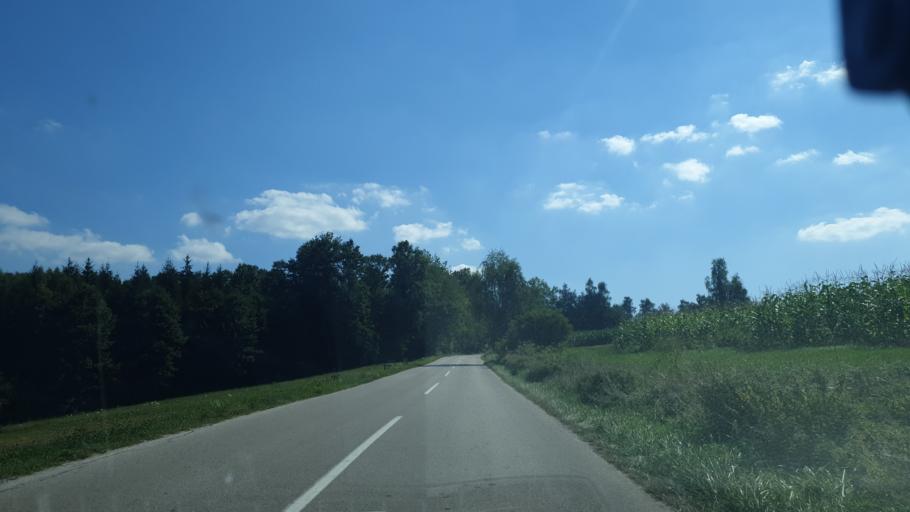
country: RS
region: Central Serbia
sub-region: Zlatiborski Okrug
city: Kosjeric
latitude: 44.0535
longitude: 20.0322
